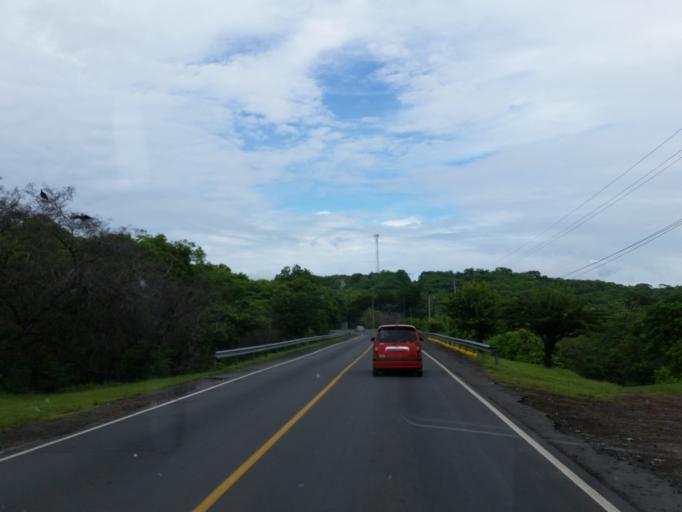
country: NI
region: Leon
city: Nagarote
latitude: 12.2432
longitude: -86.4415
